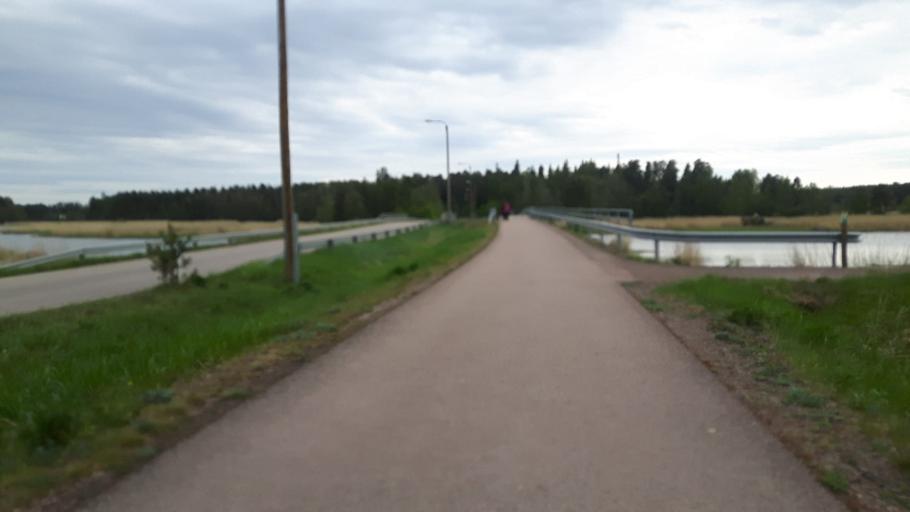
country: FI
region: Kymenlaakso
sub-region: Kotka-Hamina
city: Hamina
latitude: 60.5509
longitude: 27.2289
